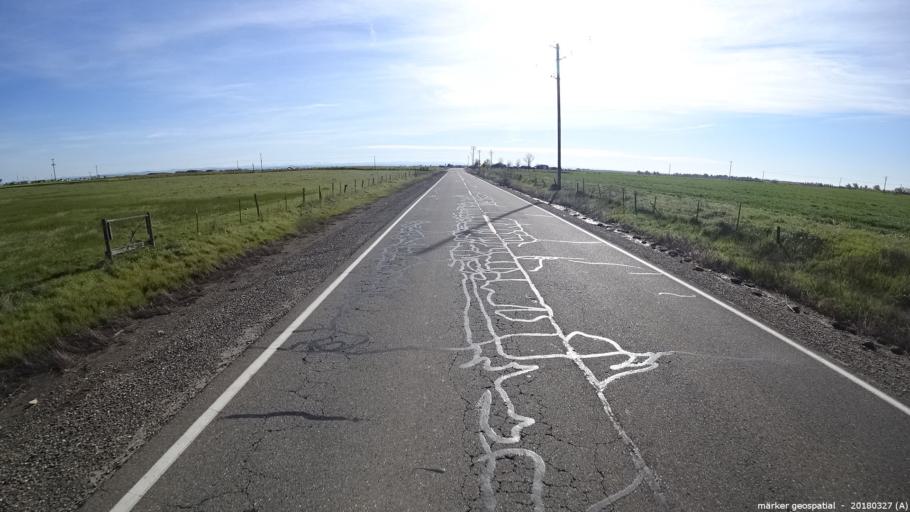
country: US
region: California
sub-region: Sacramento County
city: Wilton
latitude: 38.4967
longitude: -121.2633
